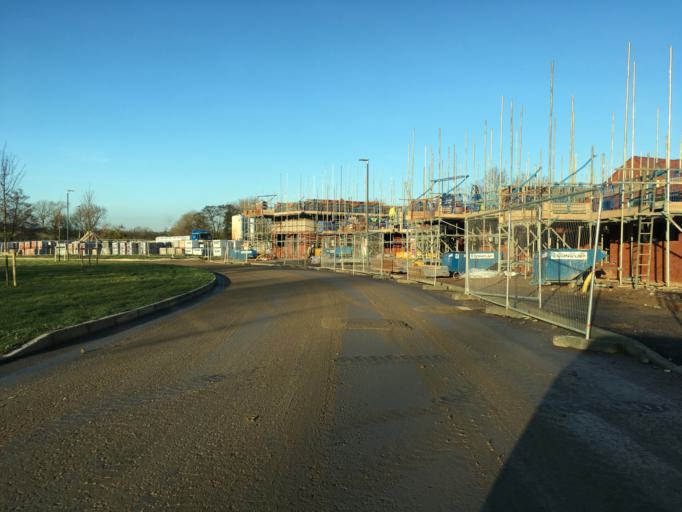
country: GB
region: England
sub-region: Gloucestershire
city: Stonehouse
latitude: 51.7560
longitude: -2.2927
